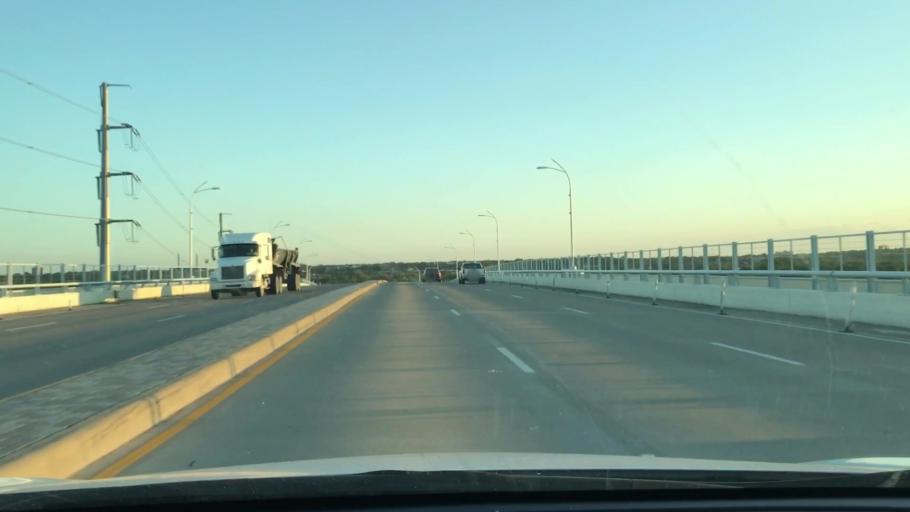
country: US
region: Texas
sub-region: Dallas County
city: Dallas
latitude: 32.7880
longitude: -96.8356
